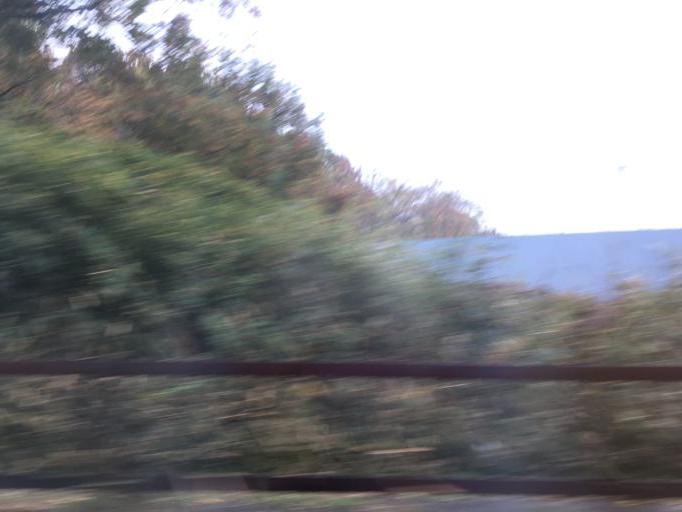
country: JP
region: Tochigi
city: Sano
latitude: 36.3267
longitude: 139.6355
